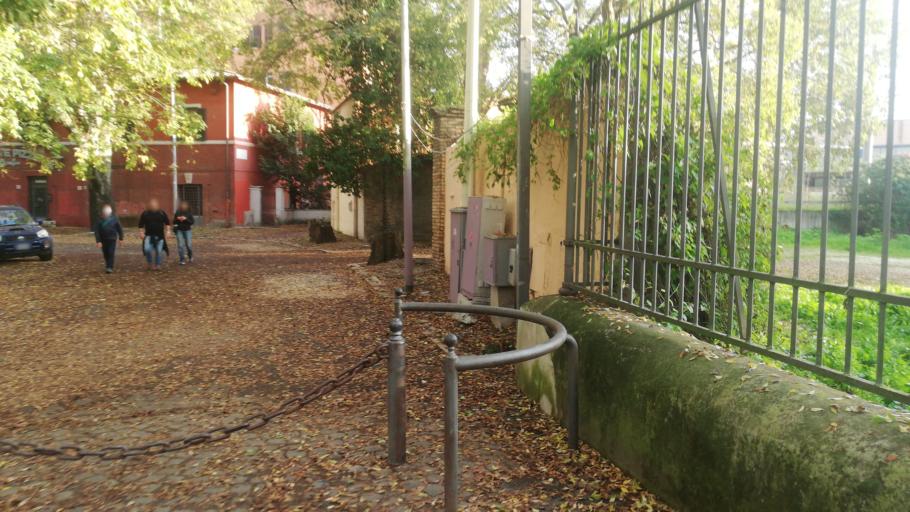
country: IT
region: Latium
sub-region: Citta metropolitana di Roma Capitale
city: Rome
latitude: 41.9336
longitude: 12.5325
